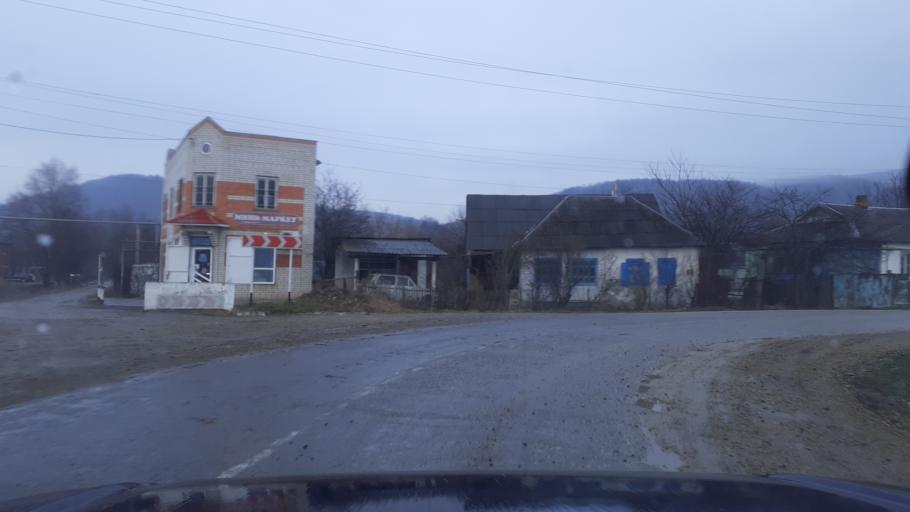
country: RU
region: Krasnodarskiy
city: Neftegorsk
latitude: 44.2984
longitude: 39.8305
